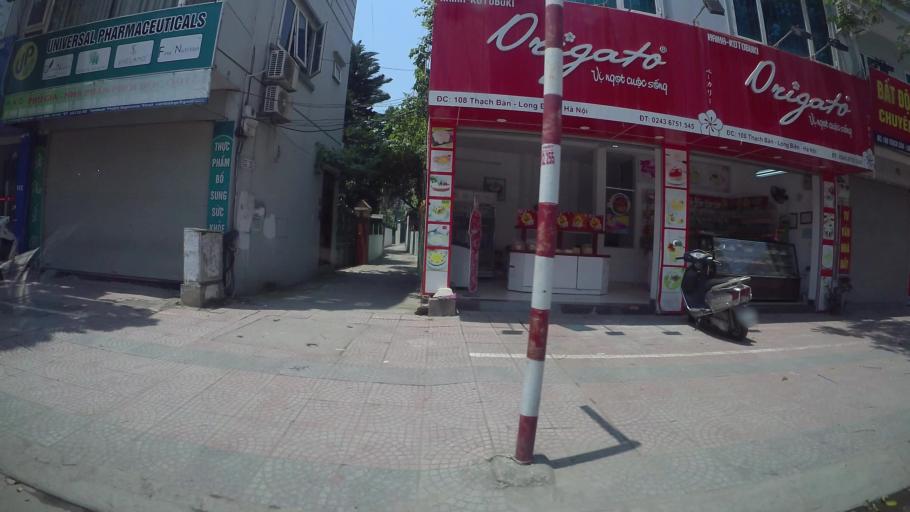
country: VN
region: Ha Noi
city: Trau Quy
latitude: 21.0259
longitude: 105.9094
